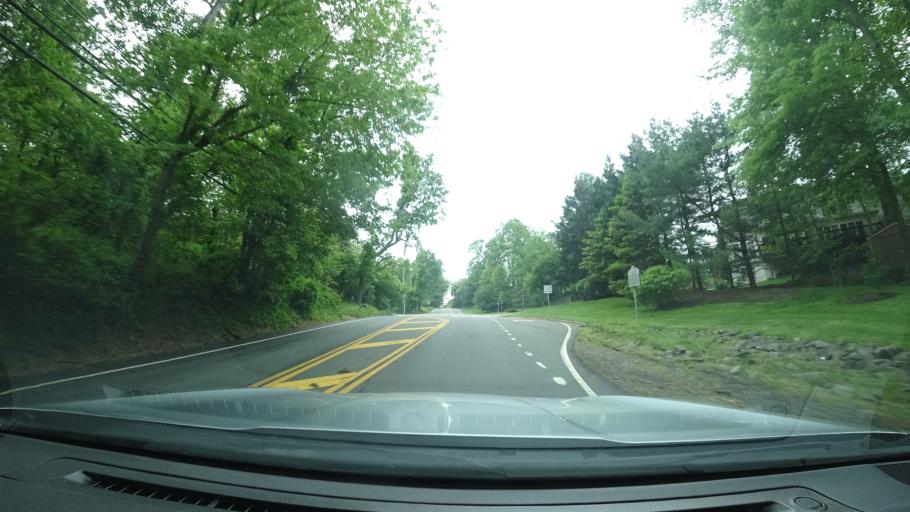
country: US
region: Virginia
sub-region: Fairfax County
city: Greenbriar
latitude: 38.8968
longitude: -77.3524
